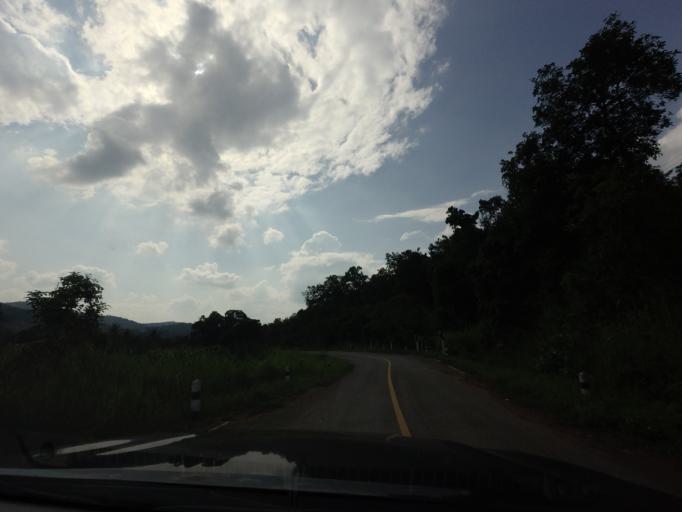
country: TH
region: Uttaradit
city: Ban Khok
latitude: 18.2307
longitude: 101.0258
